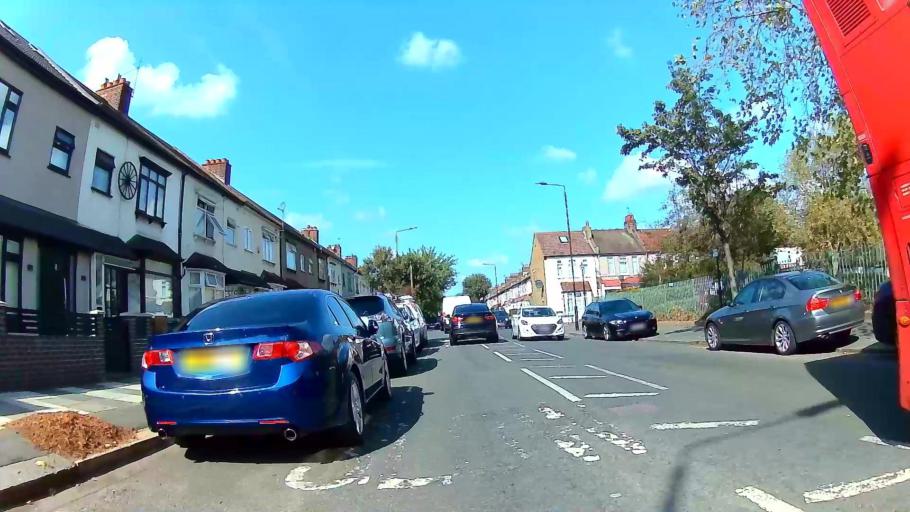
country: GB
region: England
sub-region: Greater London
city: East Ham
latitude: 51.5229
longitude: 0.0454
